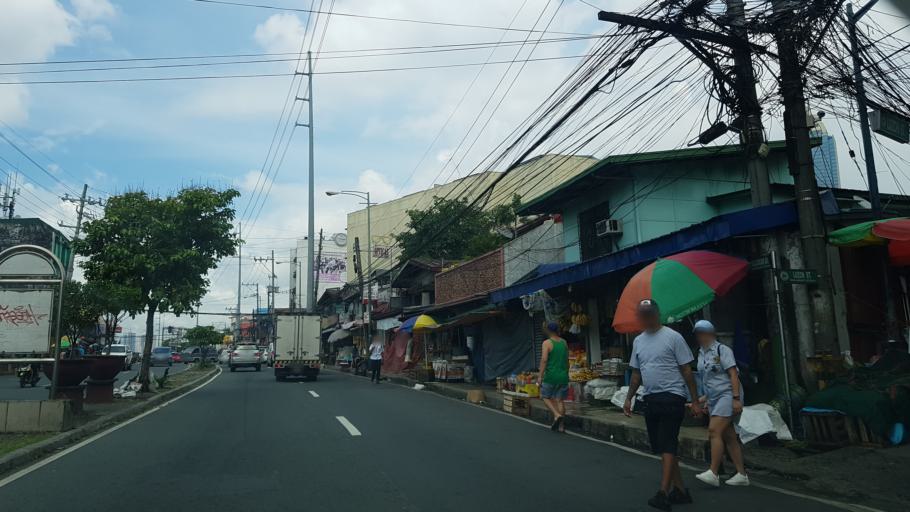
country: PH
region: Metro Manila
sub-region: Makati City
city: Makati City
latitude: 14.5580
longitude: 121.0451
